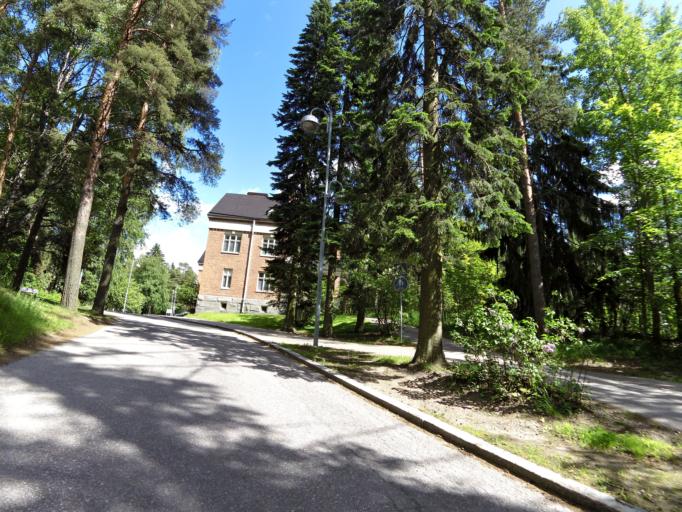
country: FI
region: Pirkanmaa
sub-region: Tampere
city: Tampere
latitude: 61.5077
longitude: 23.7829
